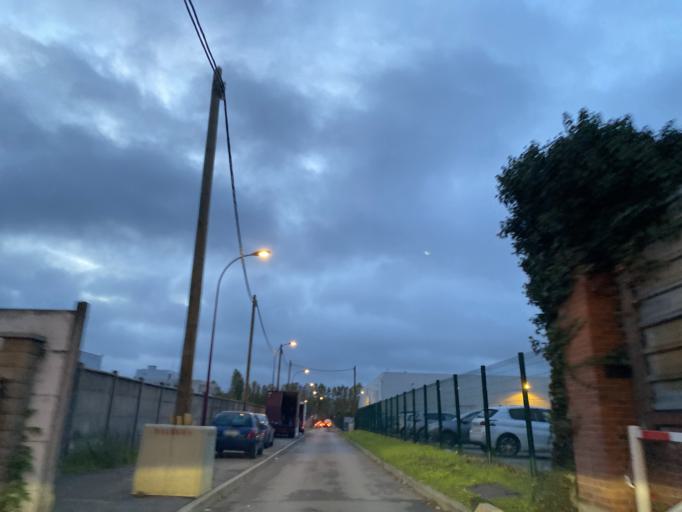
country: FR
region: Ile-de-France
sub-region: Departement du Val-d'Oise
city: Bezons
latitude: 48.9265
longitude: 2.2232
